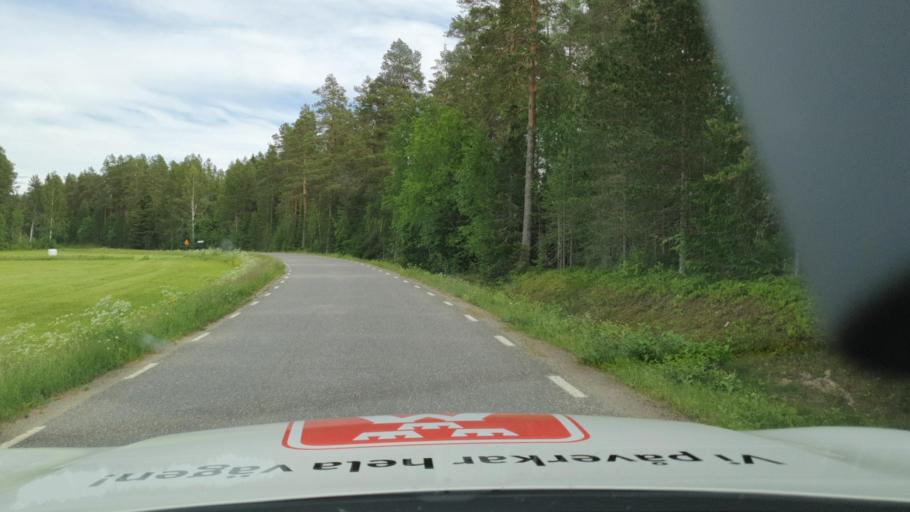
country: SE
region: Vaesterbotten
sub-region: Skelleftea Kommun
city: Burtraesk
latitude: 64.4970
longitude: 20.8717
